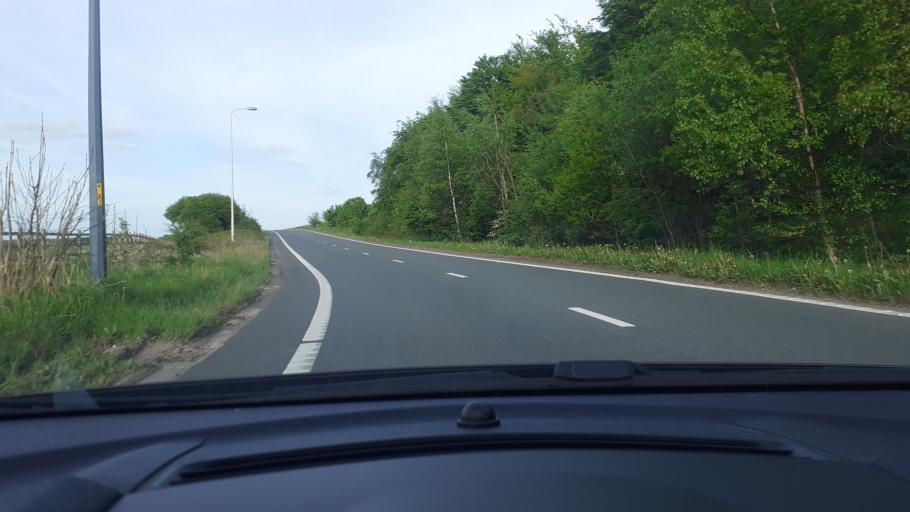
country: GB
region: England
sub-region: St. Helens
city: Rainford
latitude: 53.5372
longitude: -2.8260
